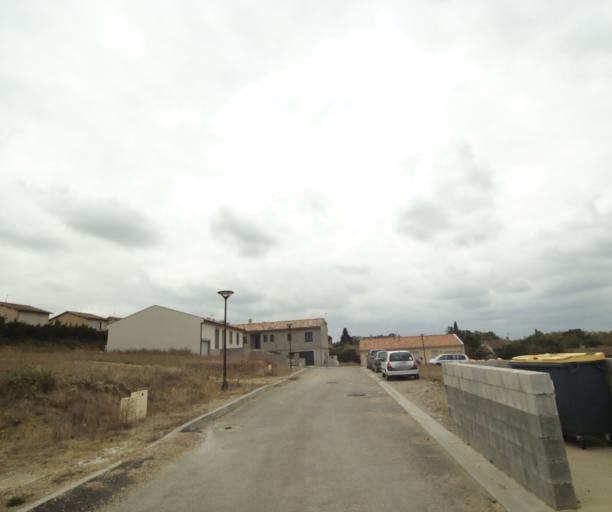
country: FR
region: Midi-Pyrenees
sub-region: Departement de la Haute-Garonne
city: Villefranche-de-Lauragais
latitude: 43.4050
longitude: 1.7201
